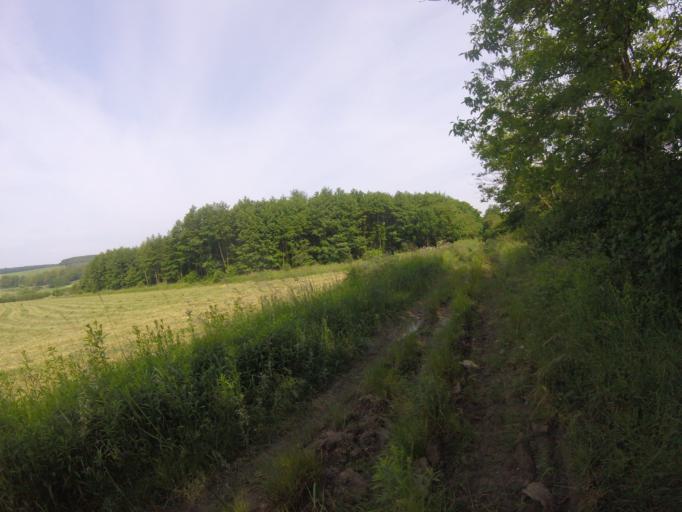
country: HU
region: Zala
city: Zalaszentgrot
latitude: 46.9068
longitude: 17.1572
